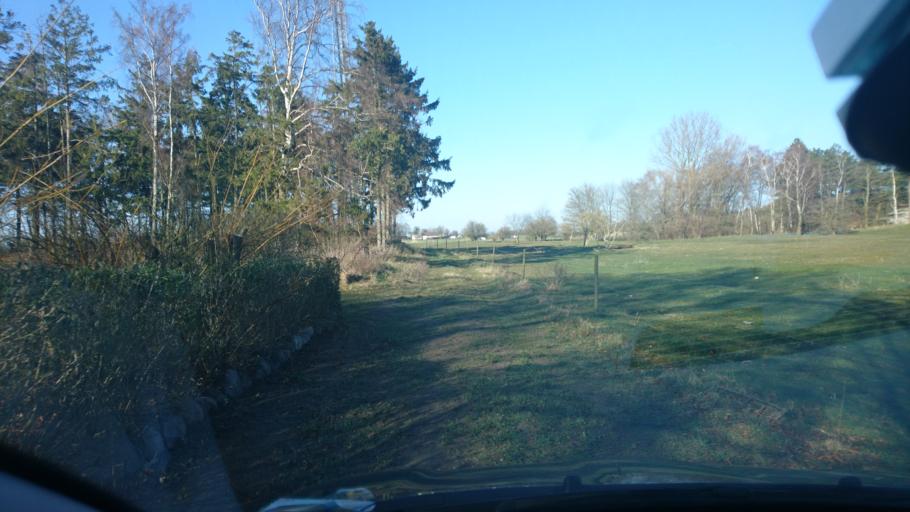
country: SE
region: Skane
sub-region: Simrishamns Kommun
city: Simrishamn
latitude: 55.4211
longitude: 14.2078
